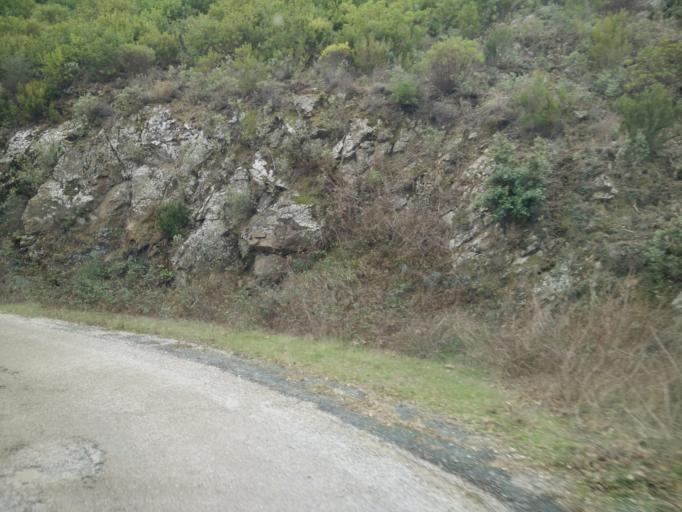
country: FR
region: Provence-Alpes-Cote d'Azur
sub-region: Departement du Var
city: Roquebrune-sur-Argens
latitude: 43.3896
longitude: 6.6103
